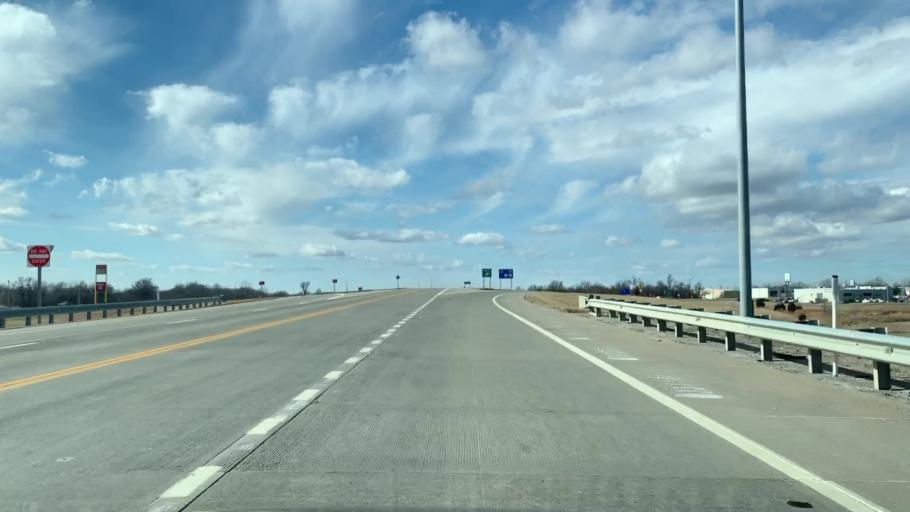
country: US
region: Kansas
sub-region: Labette County
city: Parsons
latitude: 37.3661
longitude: -95.2540
